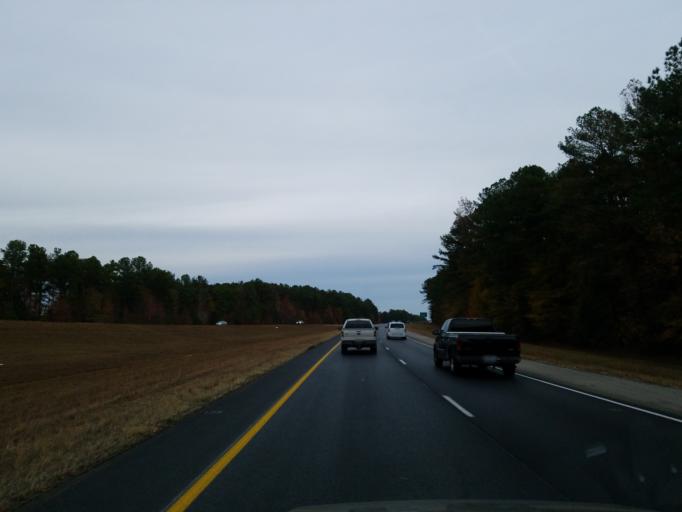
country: US
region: Mississippi
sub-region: Clarke County
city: Stonewall
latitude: 32.2613
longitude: -88.8189
